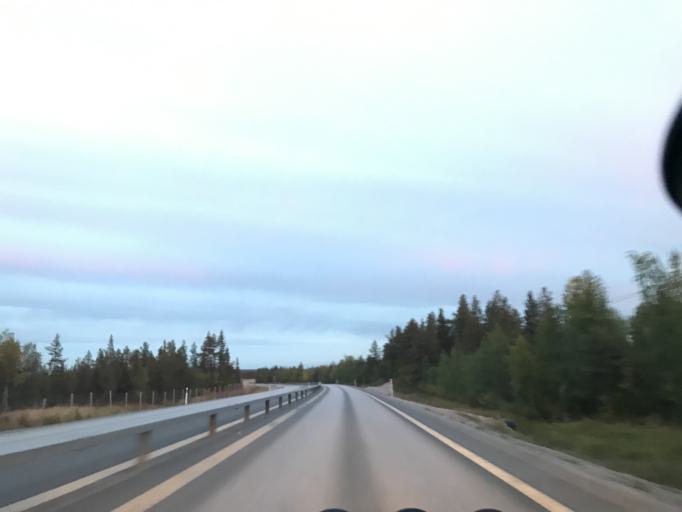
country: SE
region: Norrbotten
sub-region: Gallivare Kommun
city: Malmberget
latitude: 67.6622
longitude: 20.9953
